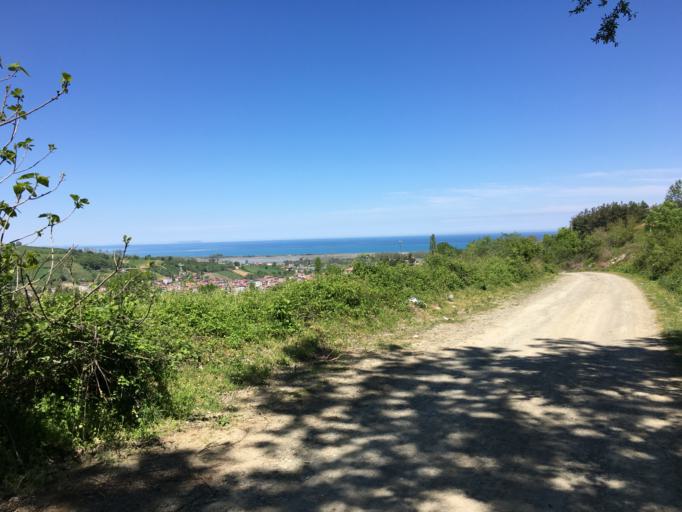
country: TR
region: Samsun
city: Alacam
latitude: 41.6027
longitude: 35.6066
